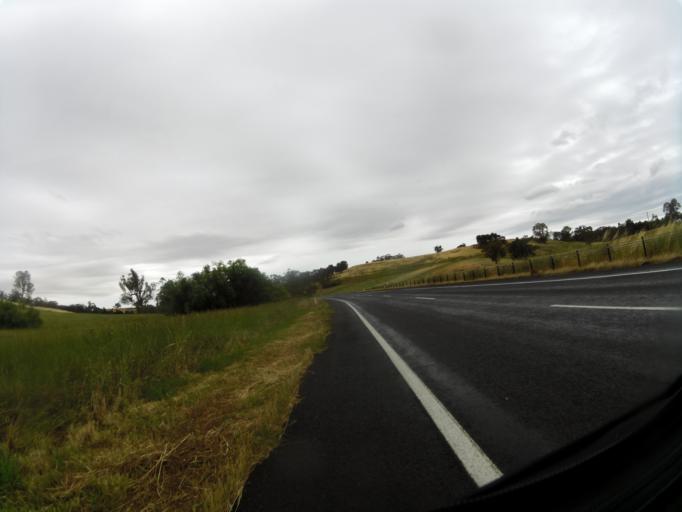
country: AU
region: Victoria
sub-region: Mount Alexander
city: Castlemaine
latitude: -37.1890
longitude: 144.0261
